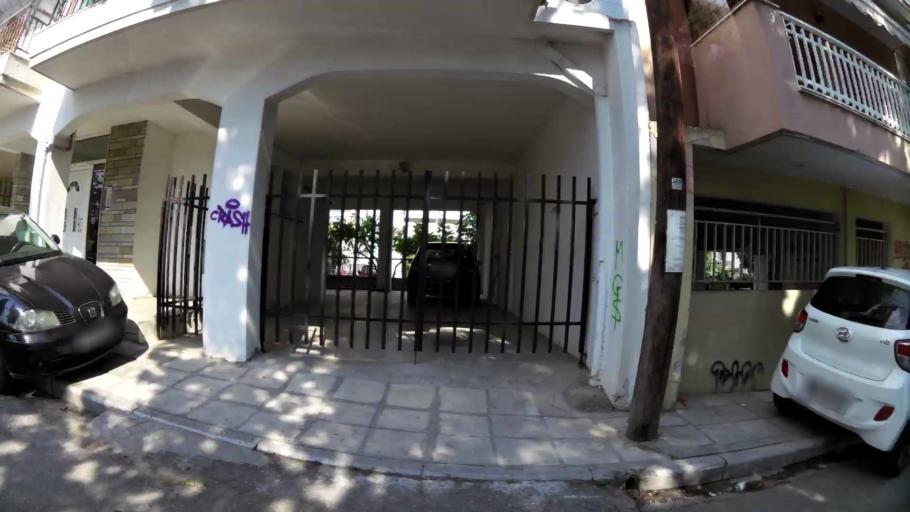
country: GR
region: Central Macedonia
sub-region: Nomos Thessalonikis
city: Polichni
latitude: 40.6610
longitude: 22.9422
